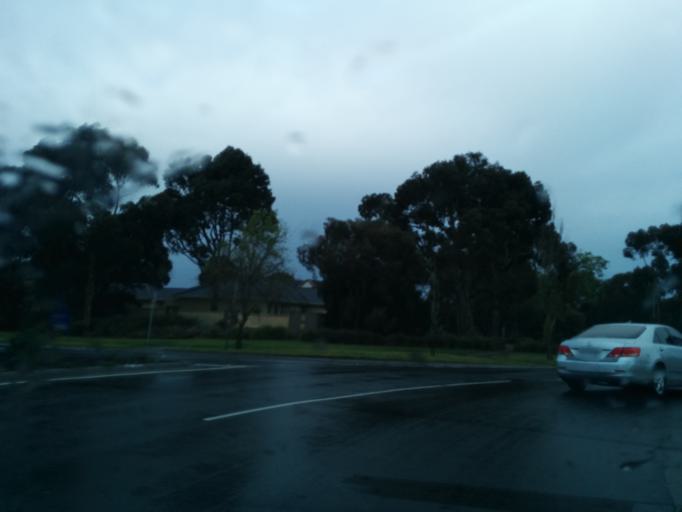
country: AU
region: Victoria
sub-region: Wyndham
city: Point Cook
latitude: -37.8966
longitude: 144.7541
